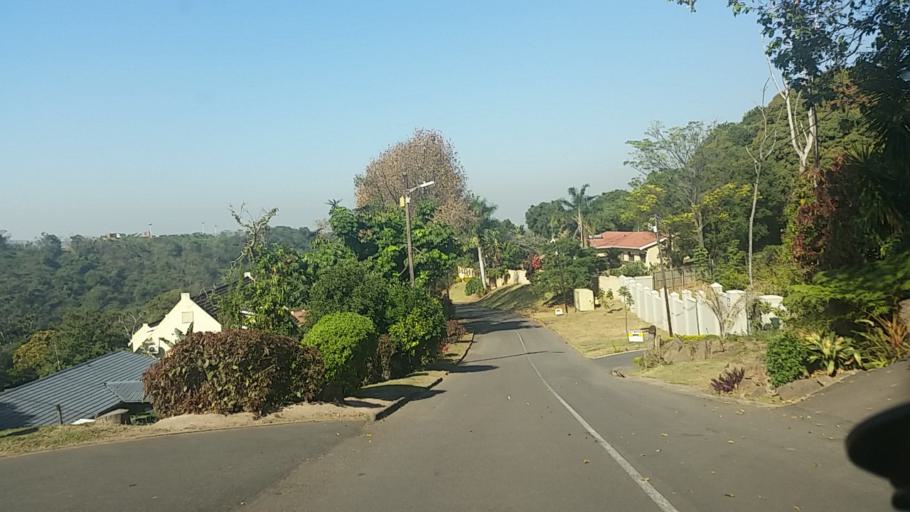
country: ZA
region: KwaZulu-Natal
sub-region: eThekwini Metropolitan Municipality
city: Berea
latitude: -29.8550
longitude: 30.9055
